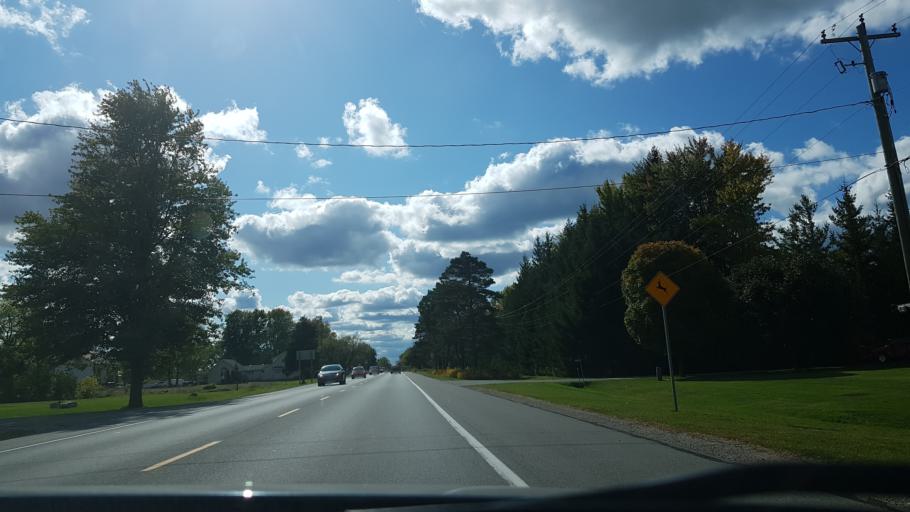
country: CA
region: Ontario
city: Bluewater
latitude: 43.3311
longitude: -81.7414
